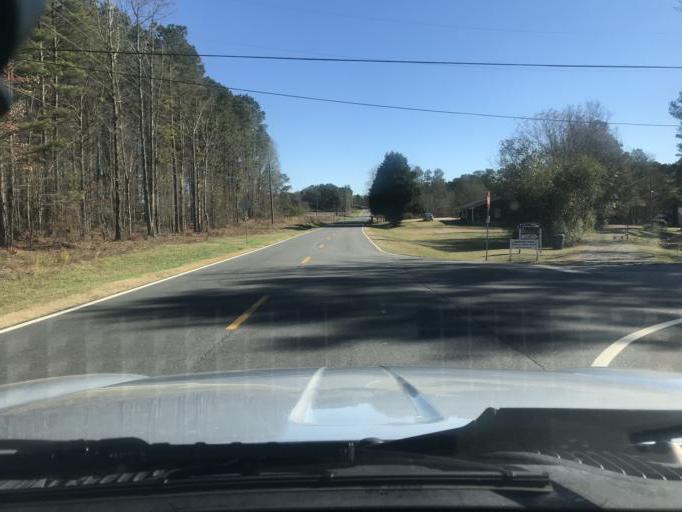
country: US
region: Georgia
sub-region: Barrow County
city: Russell
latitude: 33.9106
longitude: -83.7515
